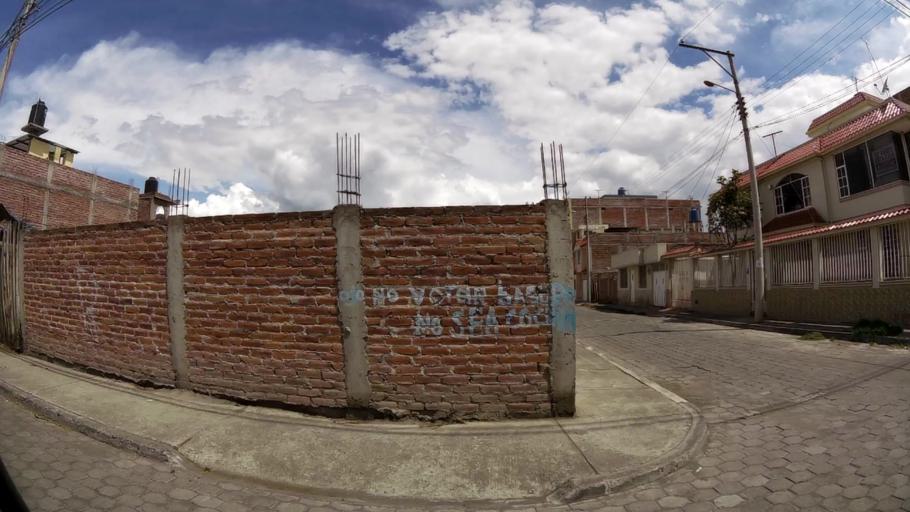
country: EC
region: Chimborazo
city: Riobamba
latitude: -1.6582
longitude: -78.6410
